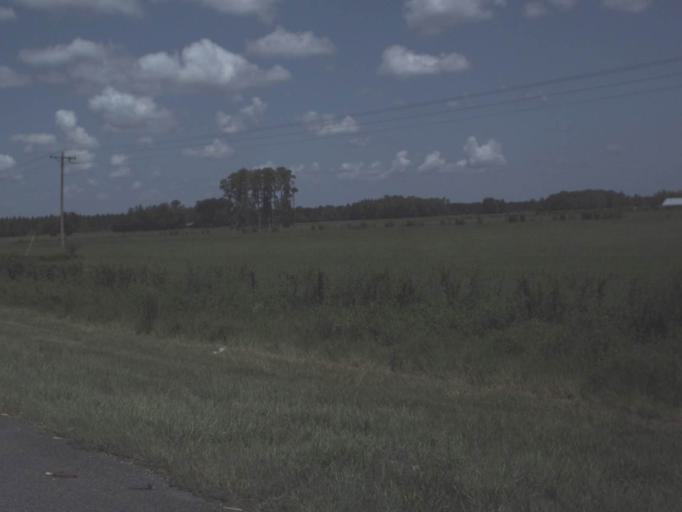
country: US
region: Florida
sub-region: Taylor County
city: Perry
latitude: 30.0843
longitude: -83.6659
